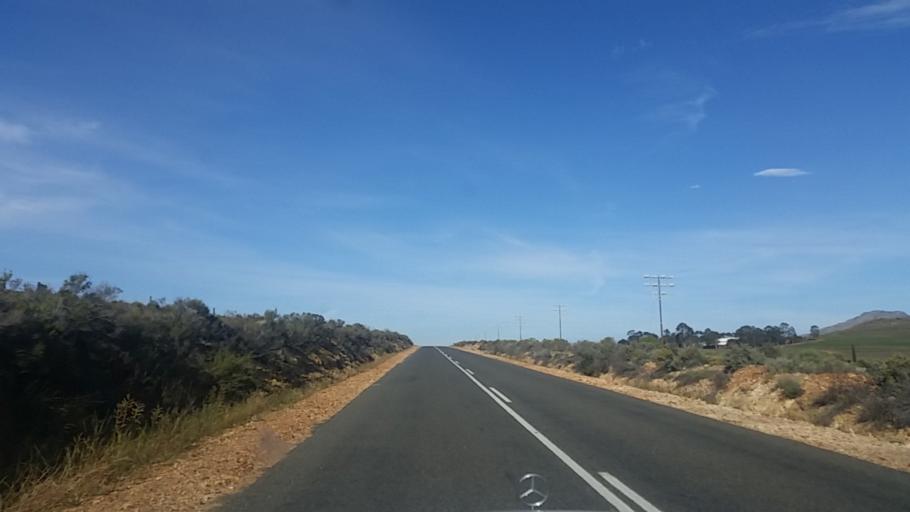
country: ZA
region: Western Cape
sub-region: Eden District Municipality
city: George
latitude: -33.7712
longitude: 22.7766
